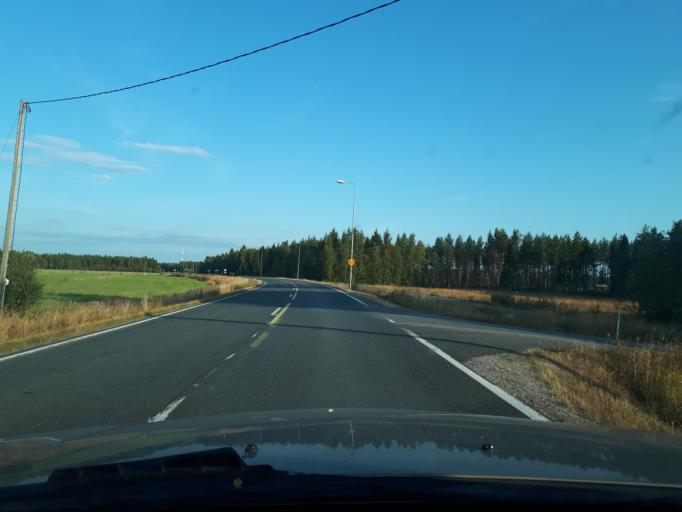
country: FI
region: Northern Ostrobothnia
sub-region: Oulu
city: Oulunsalo
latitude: 64.9807
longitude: 25.2729
